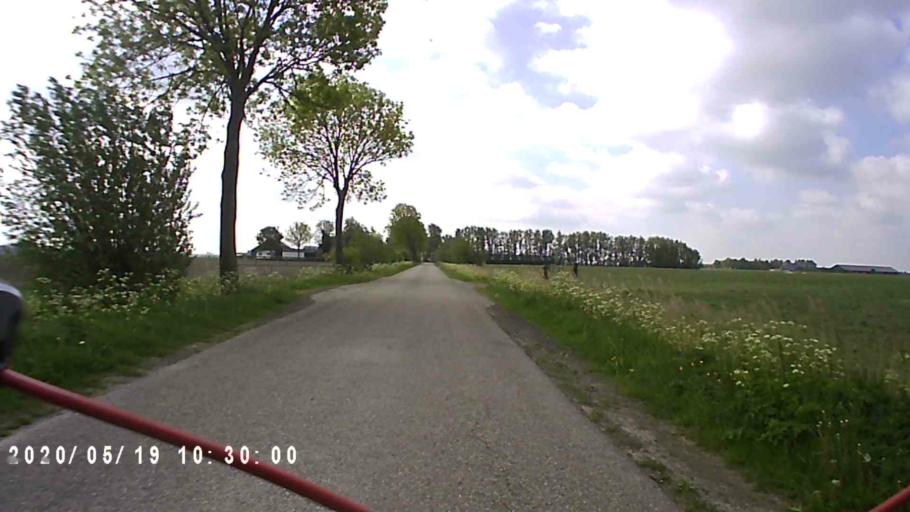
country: NL
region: Friesland
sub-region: Gemeente Kollumerland en Nieuwkruisland
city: Kollum
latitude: 53.2963
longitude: 6.1957
